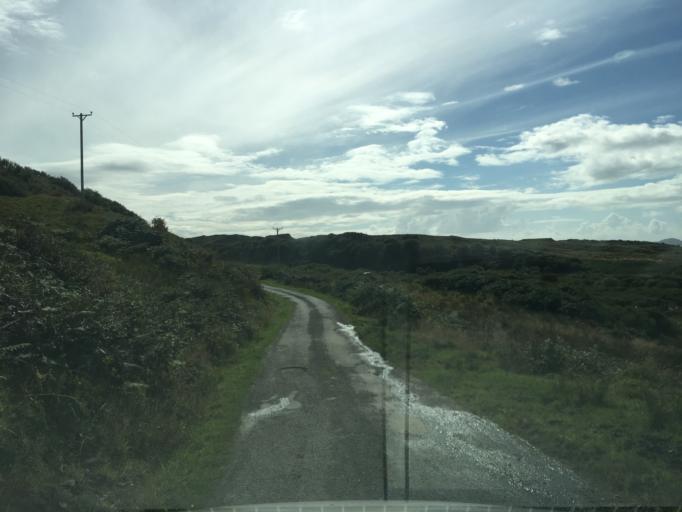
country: GB
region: Scotland
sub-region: Argyll and Bute
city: Oban
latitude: 56.2468
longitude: -5.6373
